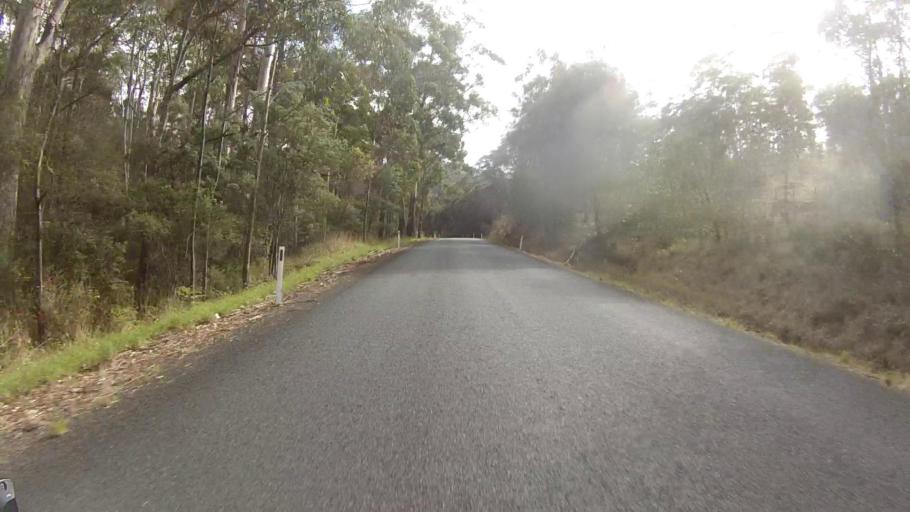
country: AU
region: Tasmania
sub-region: Sorell
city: Sorell
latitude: -42.8122
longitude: 147.7928
